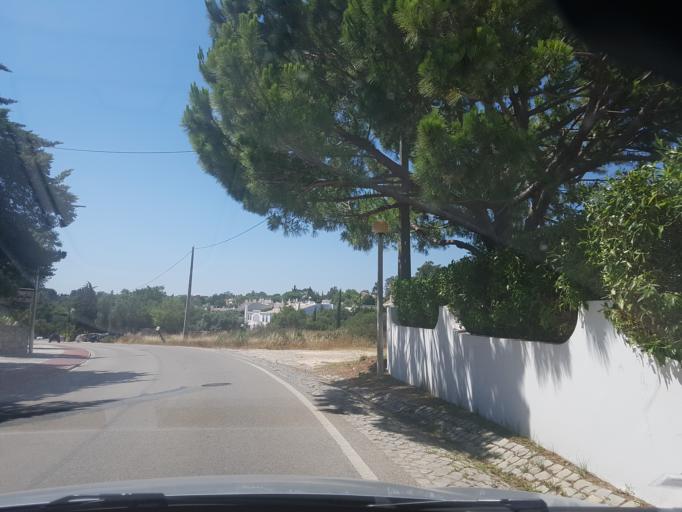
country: PT
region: Faro
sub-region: Lagoa
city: Carvoeiro
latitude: 37.0925
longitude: -8.4454
